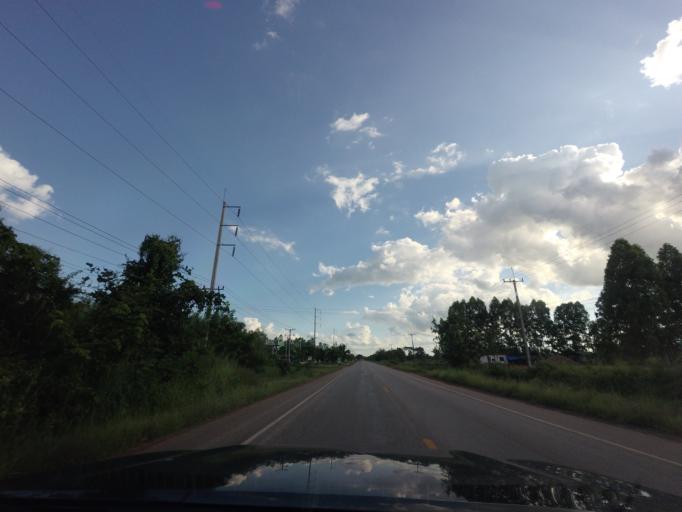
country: TH
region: Changwat Udon Thani
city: Thung Fon
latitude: 17.4794
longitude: 103.1952
